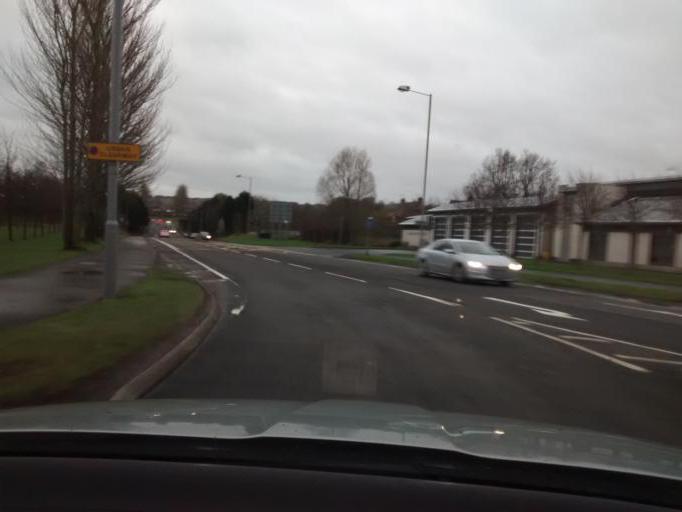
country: GB
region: Scotland
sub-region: Falkirk
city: Falkirk
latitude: 56.0036
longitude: -3.7553
